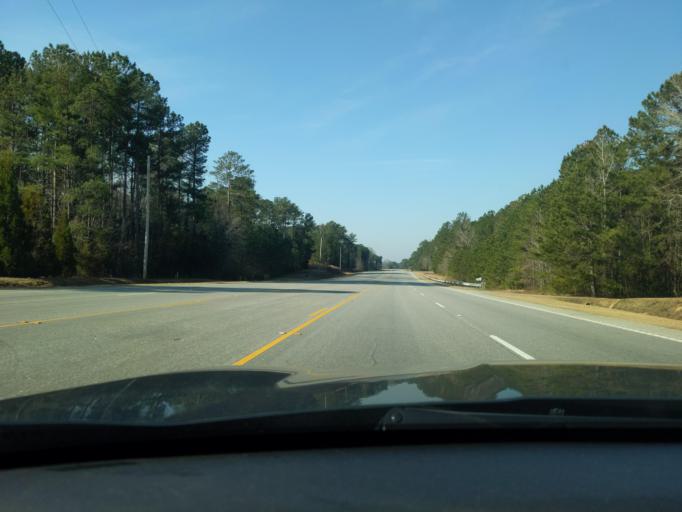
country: US
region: South Carolina
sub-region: Abbeville County
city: Abbeville
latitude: 34.1228
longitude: -82.4469
